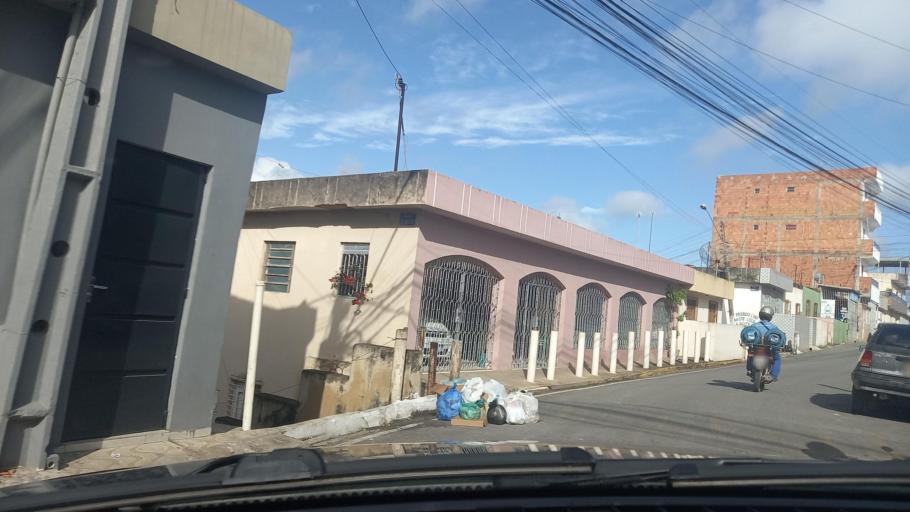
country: BR
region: Pernambuco
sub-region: Vitoria De Santo Antao
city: Vitoria de Santo Antao
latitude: -8.1186
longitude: -35.2789
